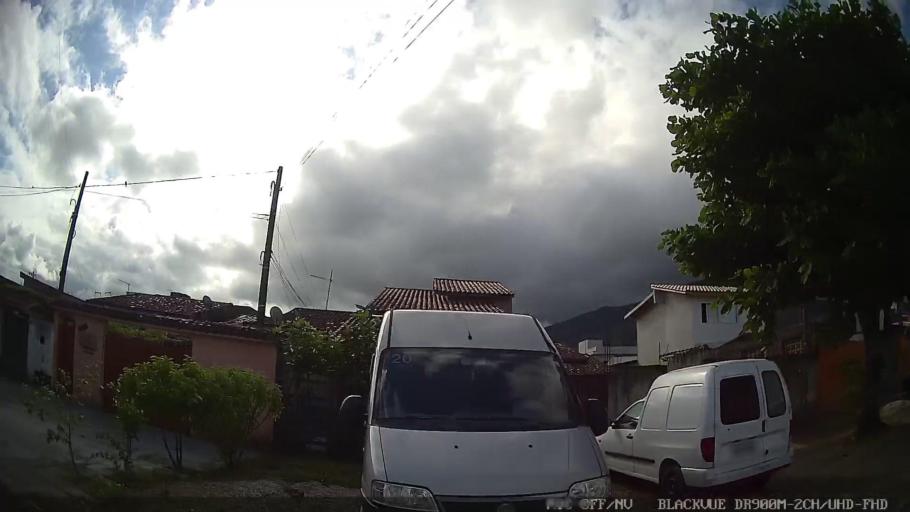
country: BR
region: Sao Paulo
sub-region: Caraguatatuba
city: Caraguatatuba
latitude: -23.6366
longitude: -45.4397
